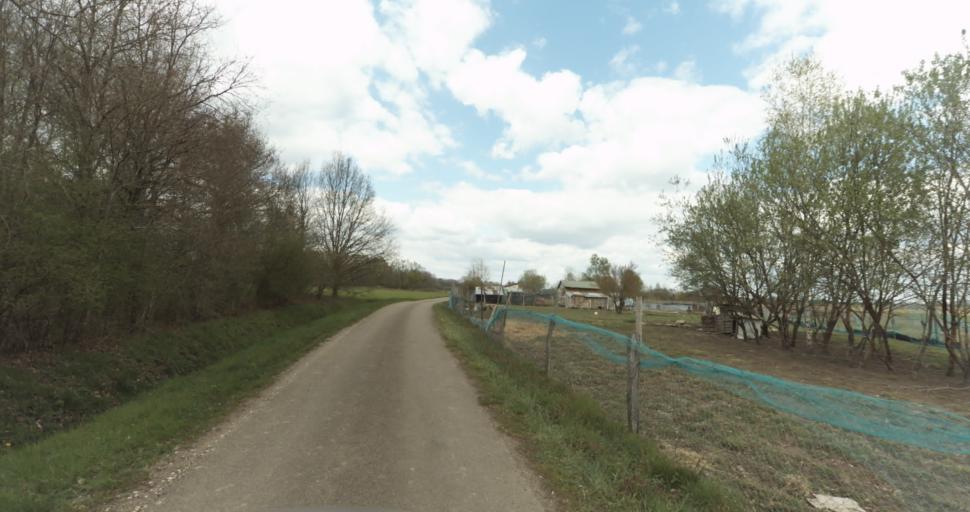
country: FR
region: Bourgogne
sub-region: Departement de la Cote-d'Or
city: Auxonne
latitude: 47.1650
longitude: 5.3956
